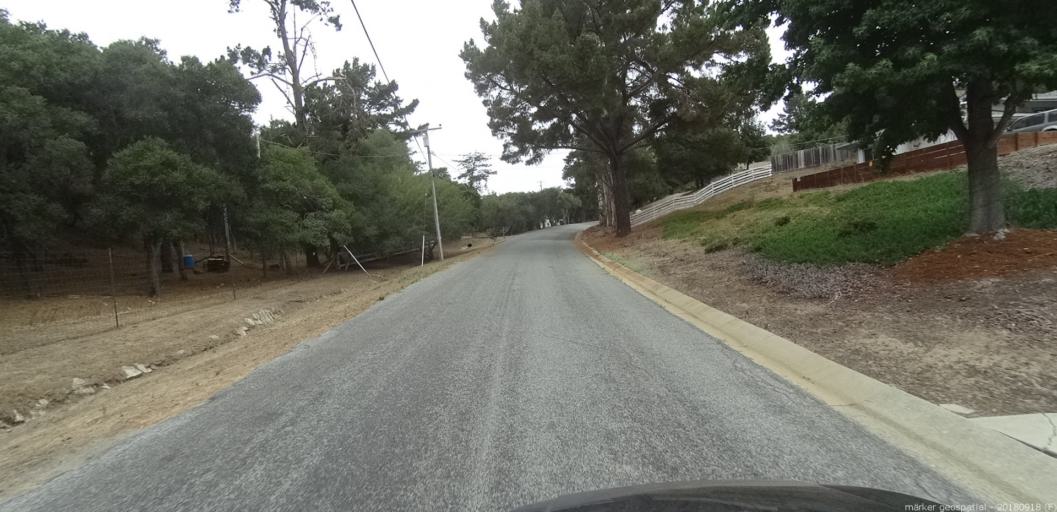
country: US
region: California
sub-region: Monterey County
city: Prunedale
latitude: 36.7857
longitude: -121.6417
